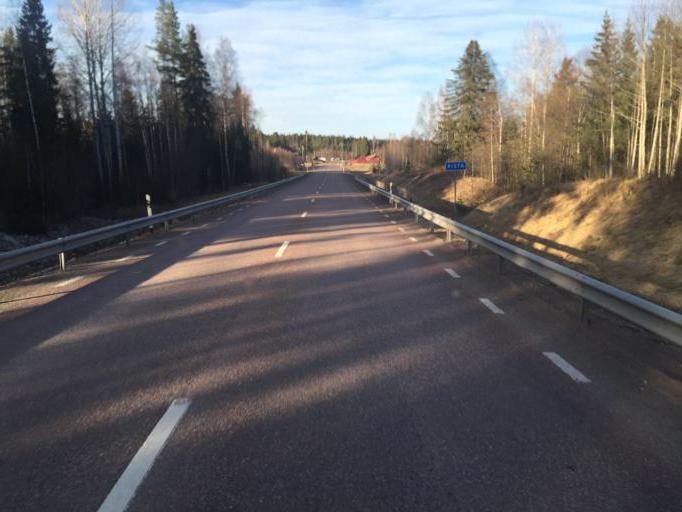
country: SE
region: Dalarna
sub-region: Gagnefs Kommun
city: Mockfjard
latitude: 60.5283
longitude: 15.0192
